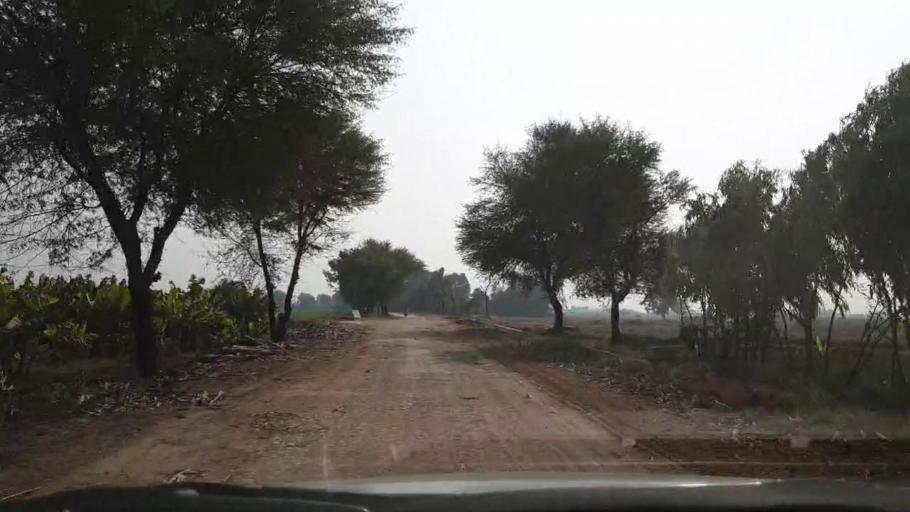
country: PK
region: Sindh
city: Matiari
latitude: 25.6590
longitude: 68.5489
